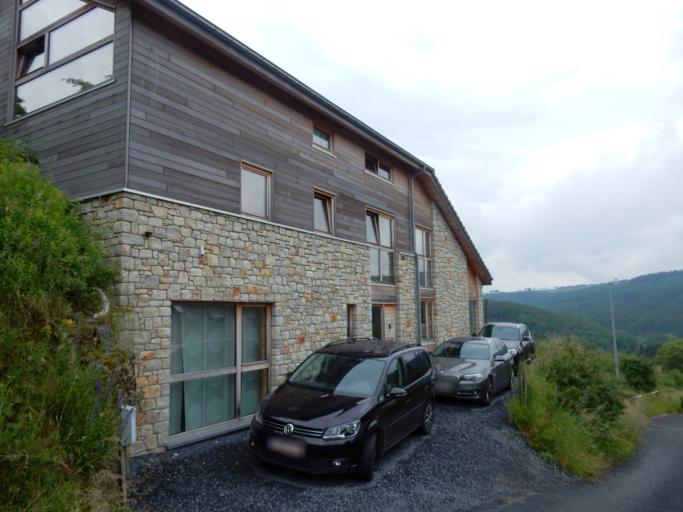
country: LU
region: Diekirch
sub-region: Canton de Wiltz
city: Esch-sur-Sure
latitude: 49.9351
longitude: 5.9338
